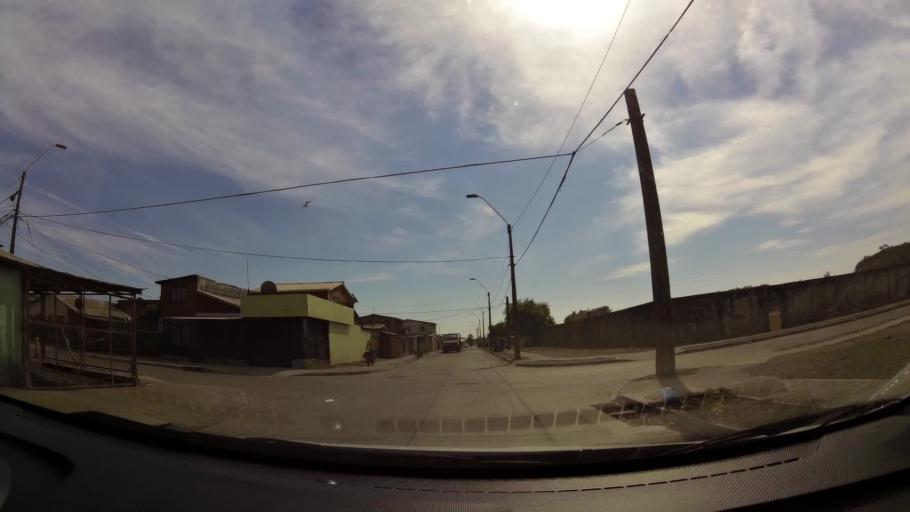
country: CL
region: Biobio
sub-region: Provincia de Concepcion
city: Talcahuano
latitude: -36.7359
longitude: -73.1149
